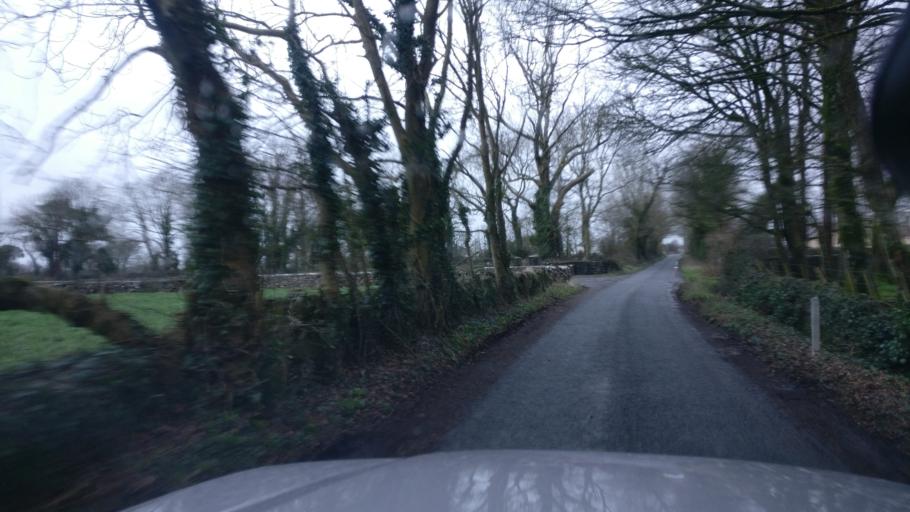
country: IE
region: Connaught
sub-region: County Galway
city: Loughrea
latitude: 53.2131
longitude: -8.6294
